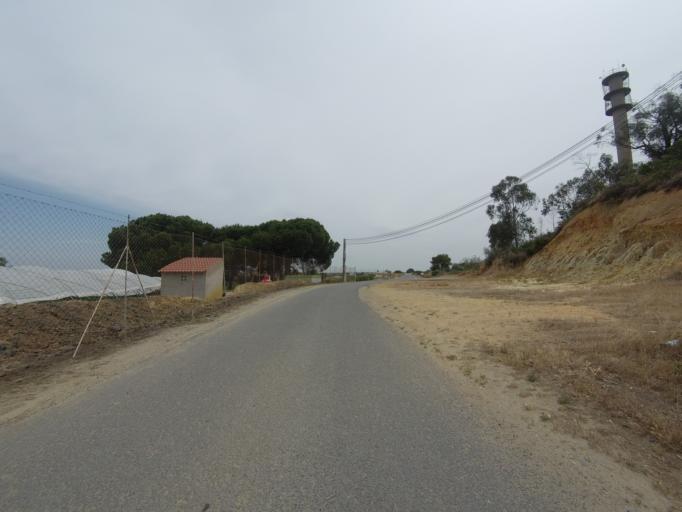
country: ES
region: Andalusia
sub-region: Provincia de Huelva
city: Palos de la Frontera
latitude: 37.2417
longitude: -6.8830
